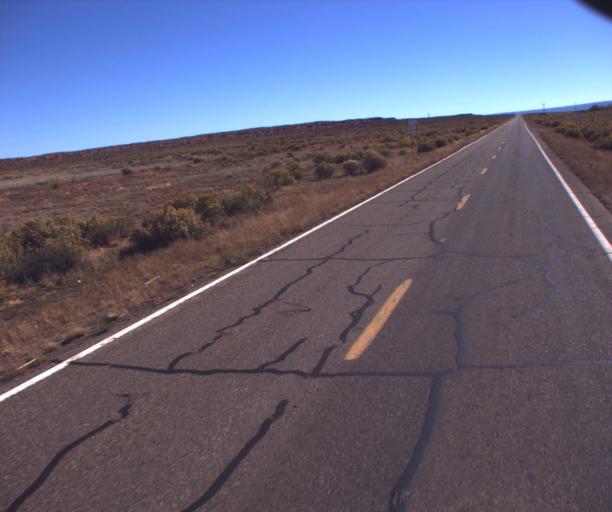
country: US
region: Arizona
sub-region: Coconino County
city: Fredonia
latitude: 36.9367
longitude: -112.5121
